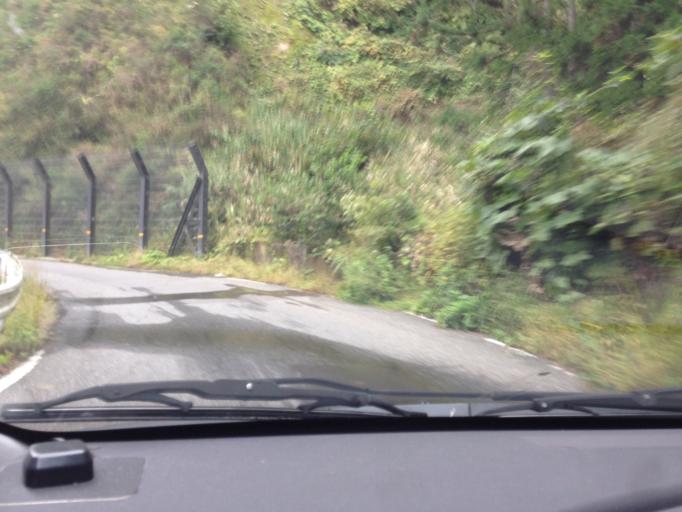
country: JP
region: Fukushima
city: Kitakata
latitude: 37.4609
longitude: 139.6458
